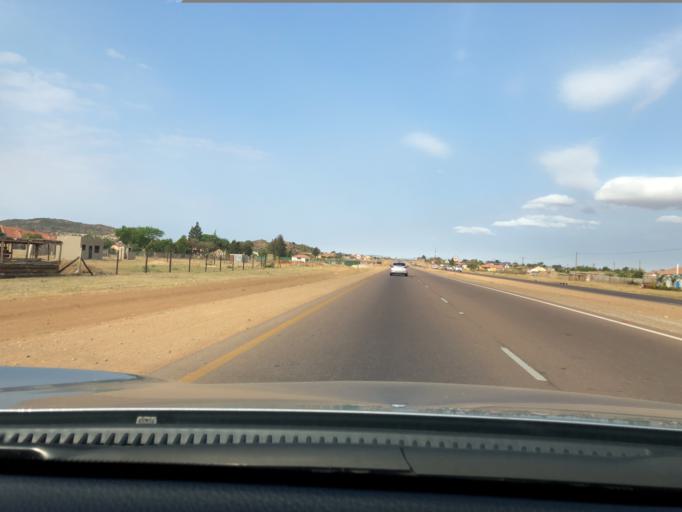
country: ZA
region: Limpopo
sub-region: Capricorn District Municipality
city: Mankoeng
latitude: -23.8922
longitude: 29.6511
